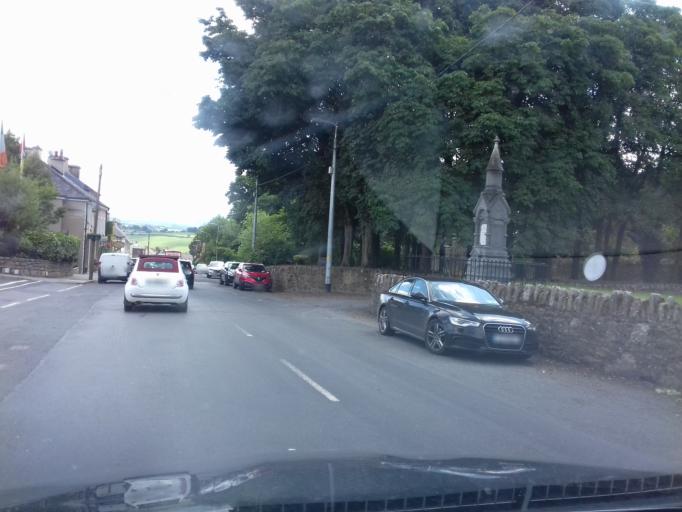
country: IE
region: Leinster
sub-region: Kilkenny
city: Graiguenamanagh
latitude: 52.6014
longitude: -6.9283
